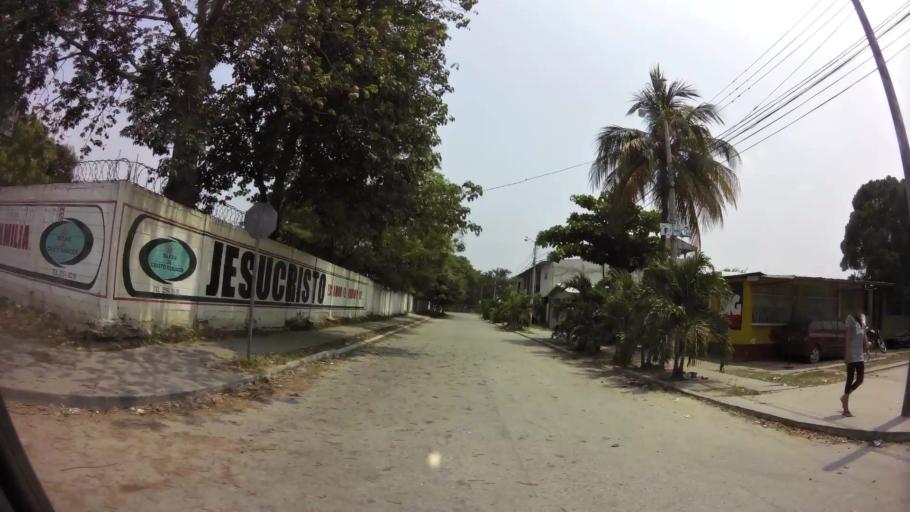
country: HN
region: Cortes
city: San Pedro Sula
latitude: 15.4893
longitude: -87.9888
